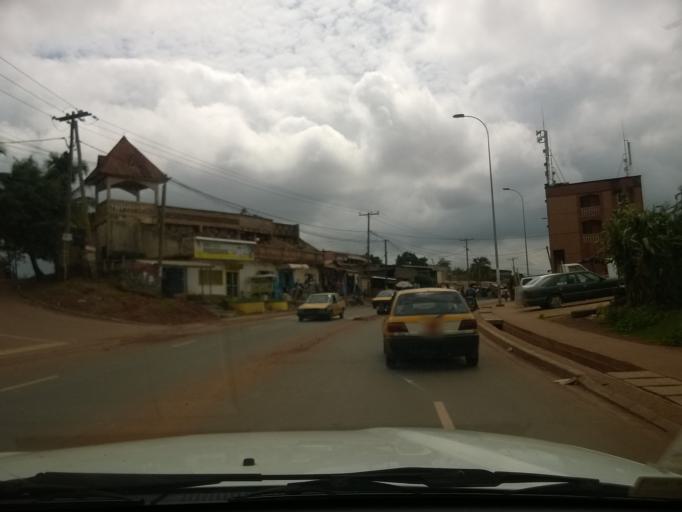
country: CM
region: Centre
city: Yaounde
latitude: 3.8328
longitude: 11.4933
